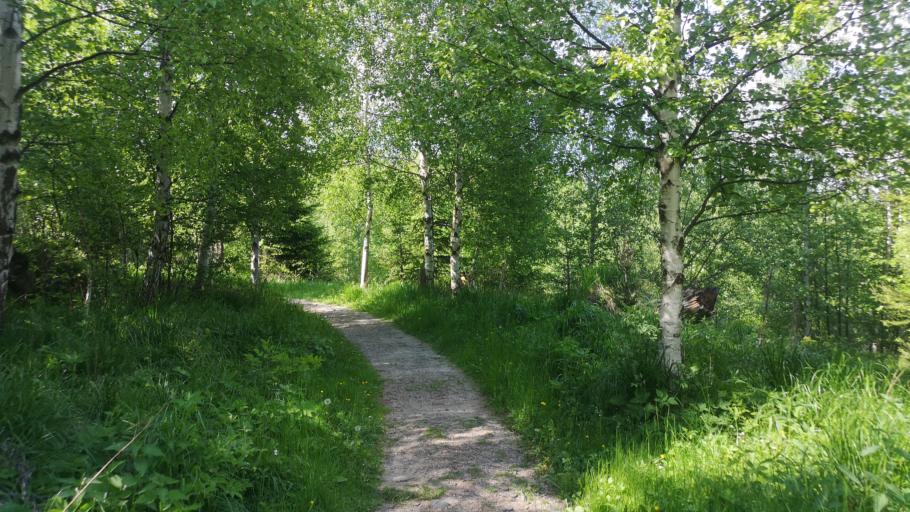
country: SK
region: Presovsky
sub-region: Okres Poprad
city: Nova Lesna
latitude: 49.1725
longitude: 20.2852
